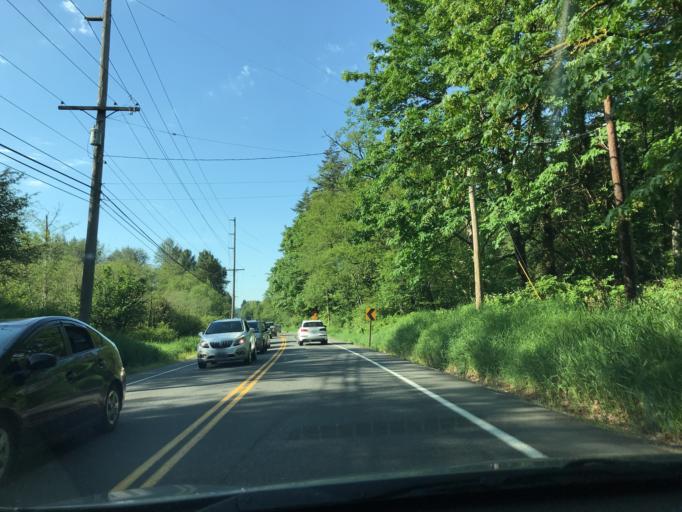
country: US
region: Washington
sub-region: King County
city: Issaquah
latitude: 47.4956
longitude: -122.0220
